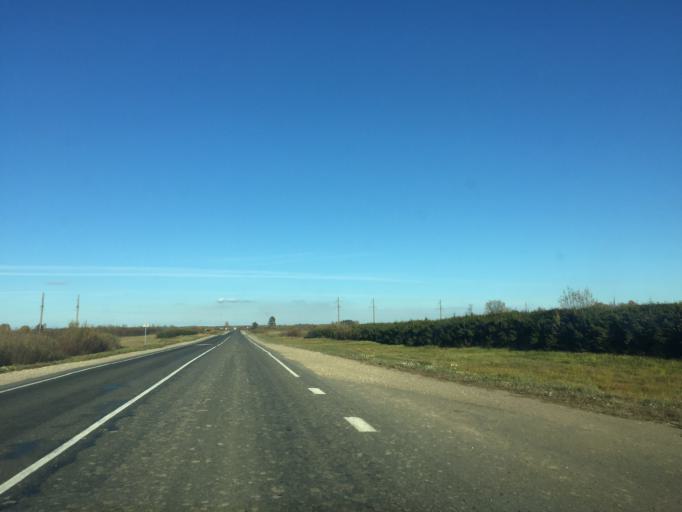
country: BY
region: Vitebsk
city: Dzisna
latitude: 55.3380
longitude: 28.2866
